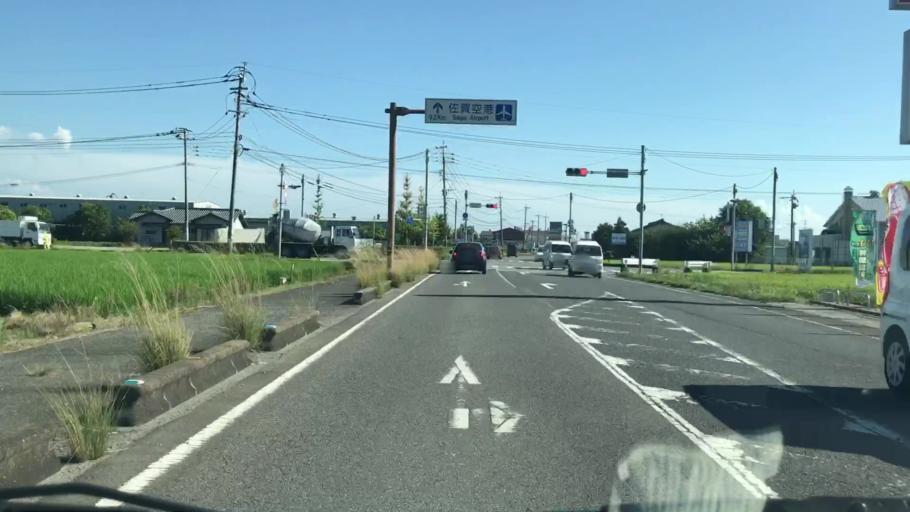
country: JP
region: Saga Prefecture
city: Okawa
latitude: 33.2133
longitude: 130.3354
